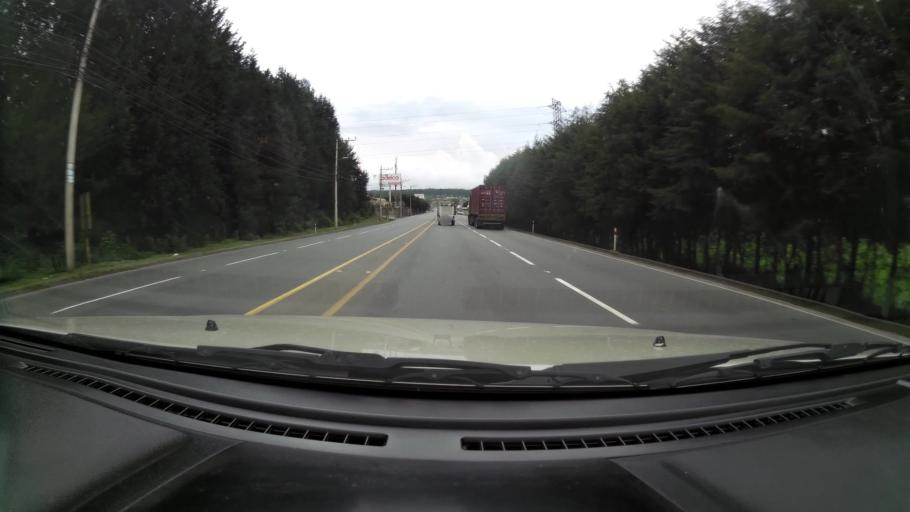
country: EC
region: Pichincha
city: Machachi
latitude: -0.4366
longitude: -78.6196
